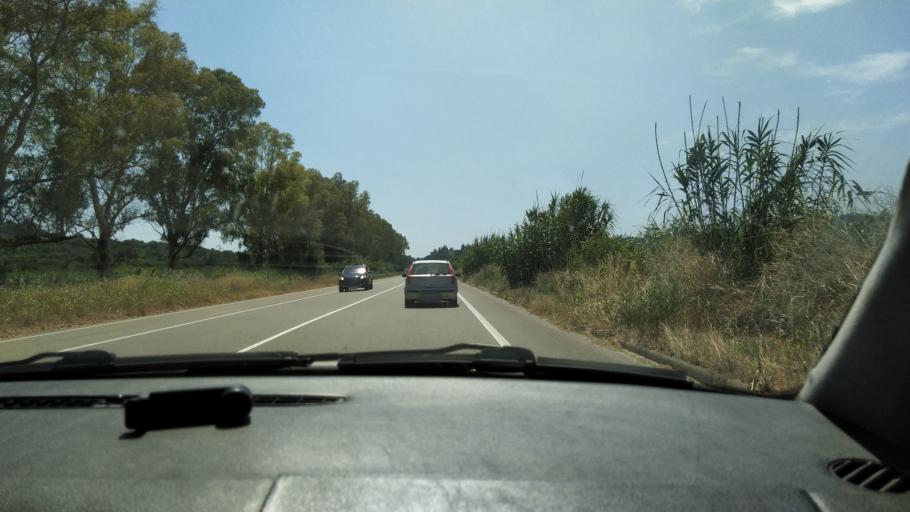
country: IT
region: Apulia
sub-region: Provincia di Taranto
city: Marina di Ginosa
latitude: 40.4381
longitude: 16.7859
